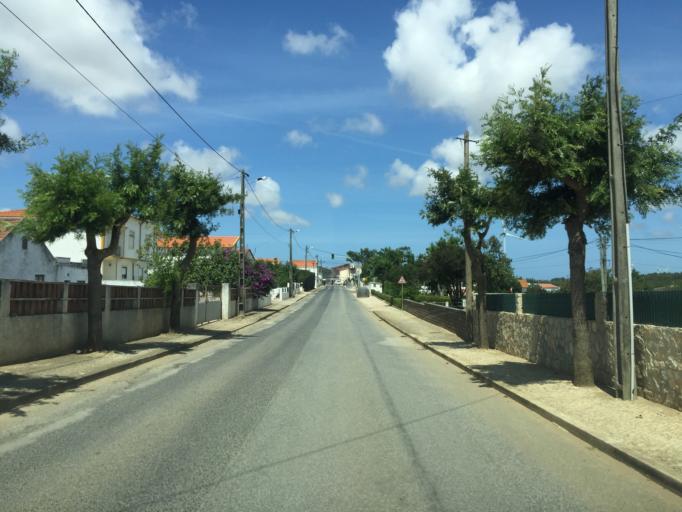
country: PT
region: Lisbon
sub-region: Lourinha
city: Lourinha
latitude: 39.2737
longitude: -9.2763
